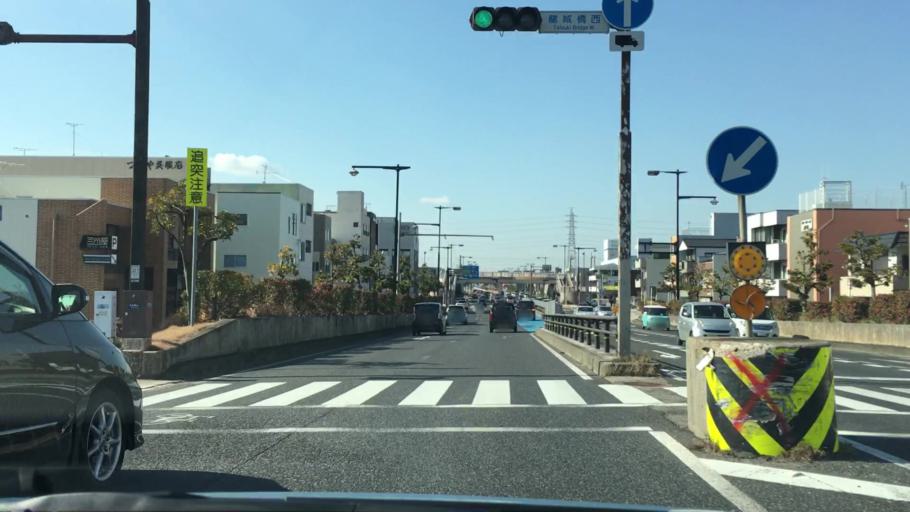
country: JP
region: Aichi
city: Okazaki
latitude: 34.9585
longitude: 137.1577
